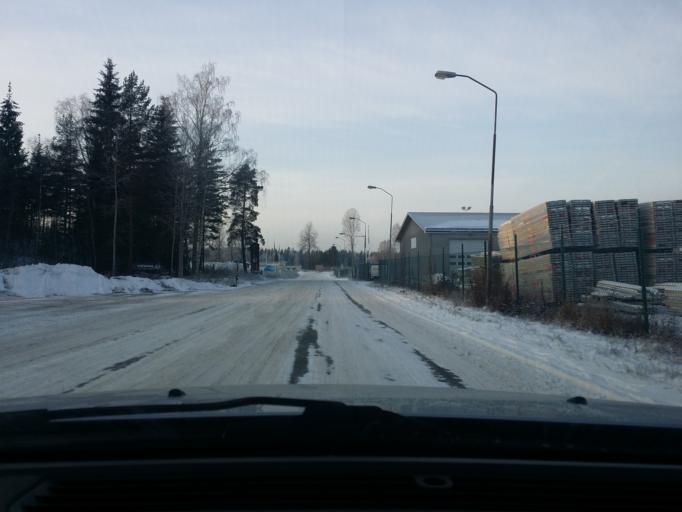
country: SE
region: OErebro
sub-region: Lindesbergs Kommun
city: Lindesberg
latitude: 59.5992
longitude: 15.1992
